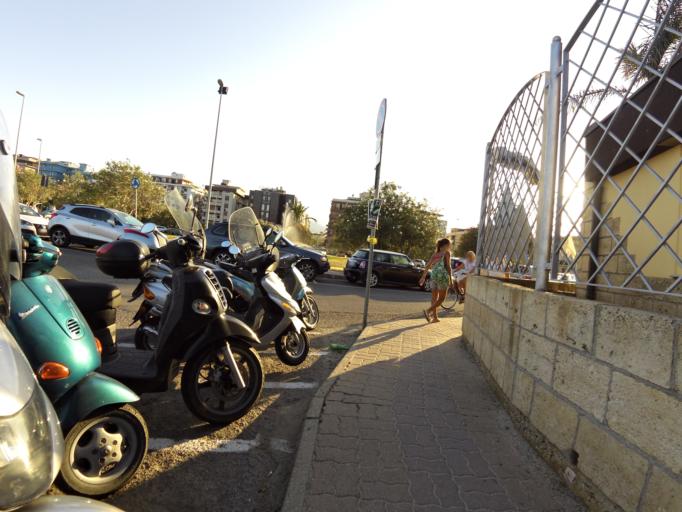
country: IT
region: Calabria
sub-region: Provincia di Catanzaro
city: Soverato Marina
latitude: 38.6881
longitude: 16.5552
